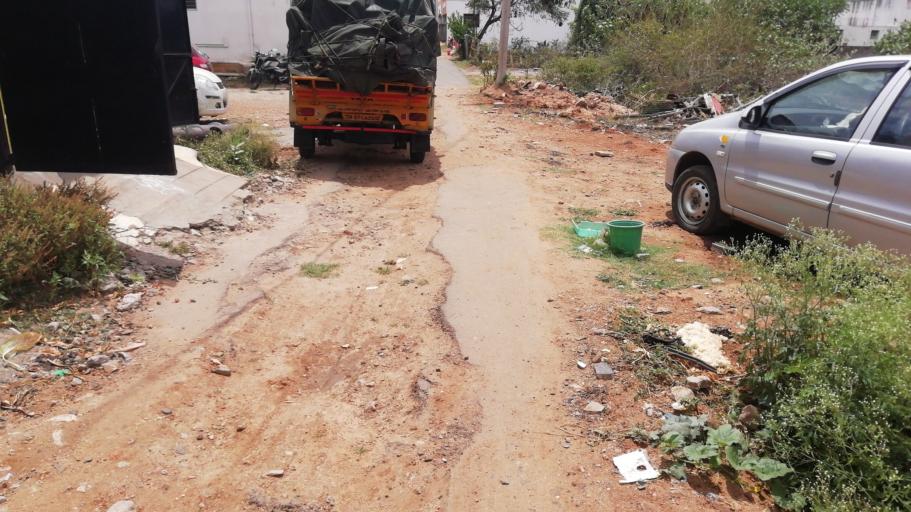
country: IN
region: Tamil Nadu
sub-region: Coimbatore
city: Coimbatore
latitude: 10.9913
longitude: 76.9808
